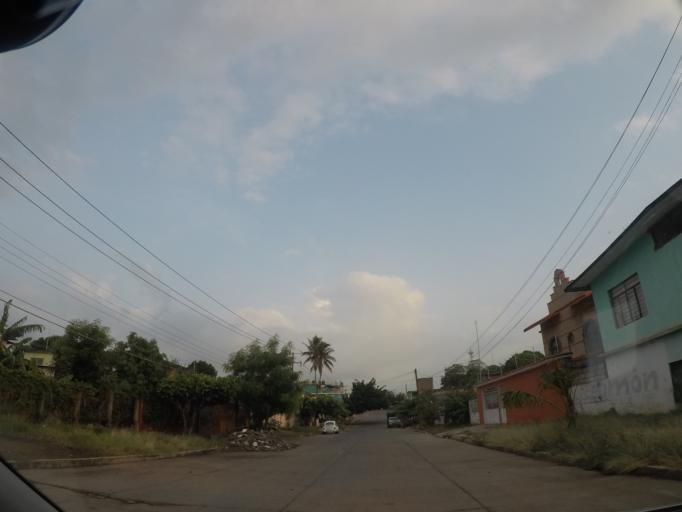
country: MX
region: Oaxaca
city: Matias Romero
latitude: 16.8740
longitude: -95.0374
